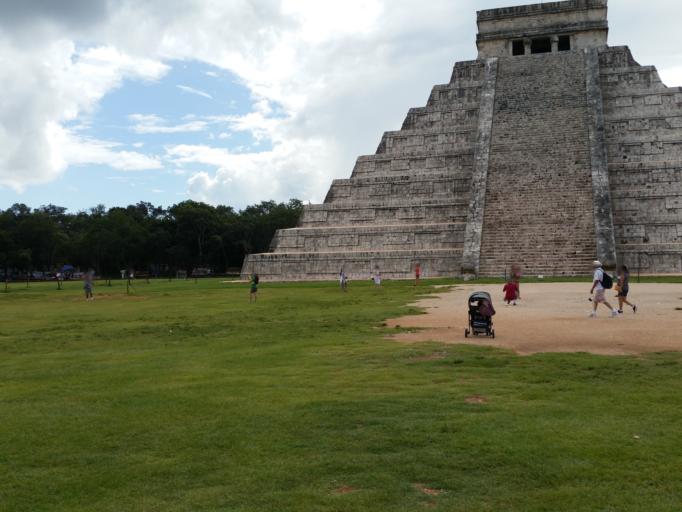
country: MX
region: Yucatan
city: Chichen-Itza
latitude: 20.6837
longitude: -88.5683
